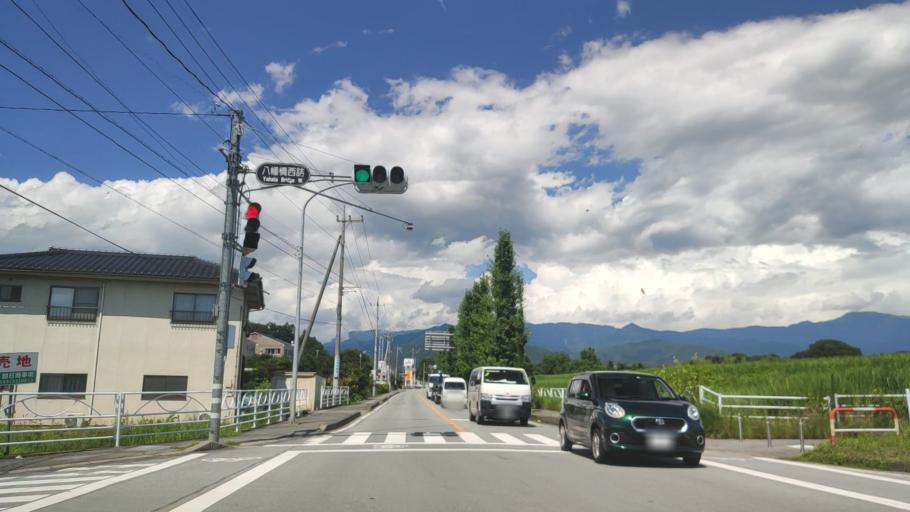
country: JP
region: Yamanashi
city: Enzan
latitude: 35.7037
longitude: 138.6930
